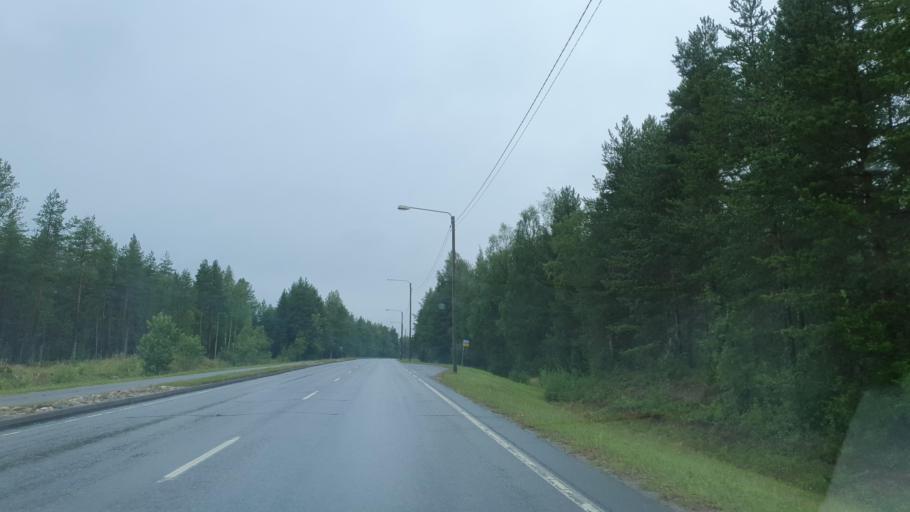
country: FI
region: Lapland
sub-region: Itae-Lappi
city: Kemijaervi
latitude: 66.7130
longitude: 27.4987
